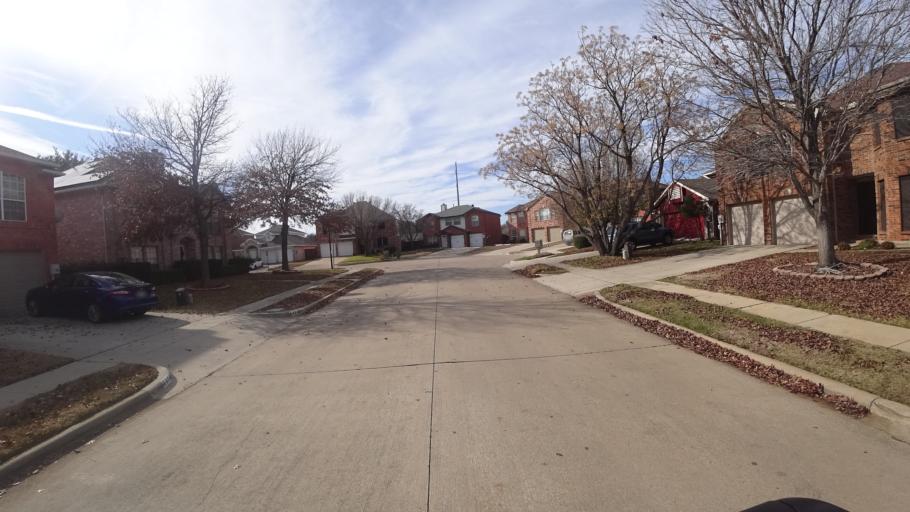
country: US
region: Texas
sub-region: Denton County
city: Highland Village
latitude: 33.0692
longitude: -97.0344
